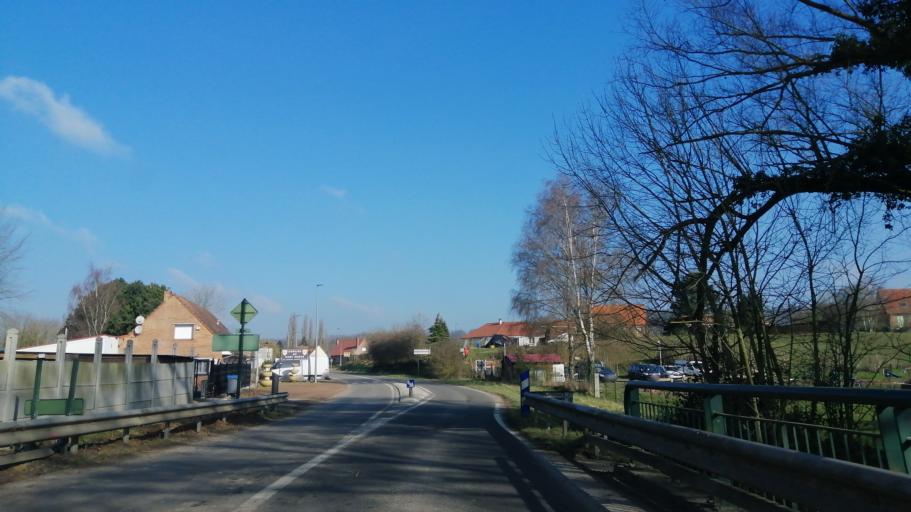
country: FR
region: Nord-Pas-de-Calais
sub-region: Departement du Pas-de-Calais
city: Ranchicourt
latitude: 50.4317
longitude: 2.5605
